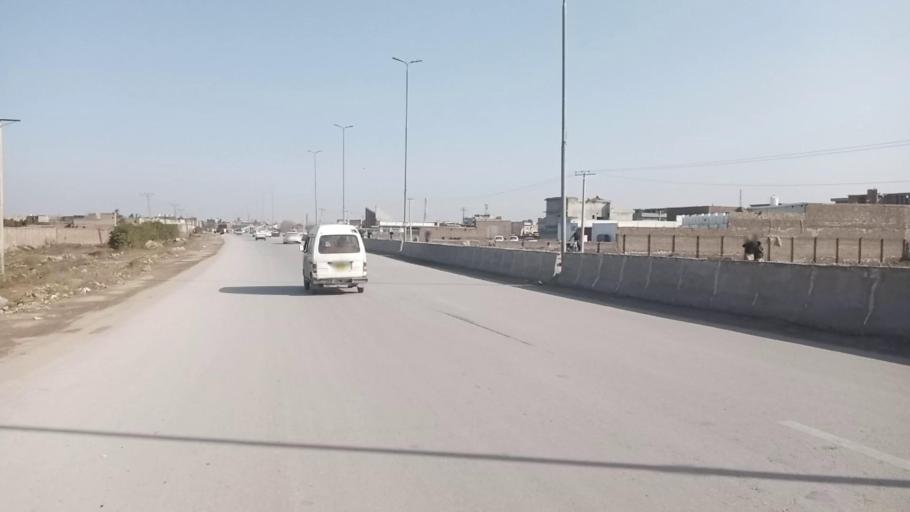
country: PK
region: Khyber Pakhtunkhwa
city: Peshawar
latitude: 34.0339
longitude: 71.5676
